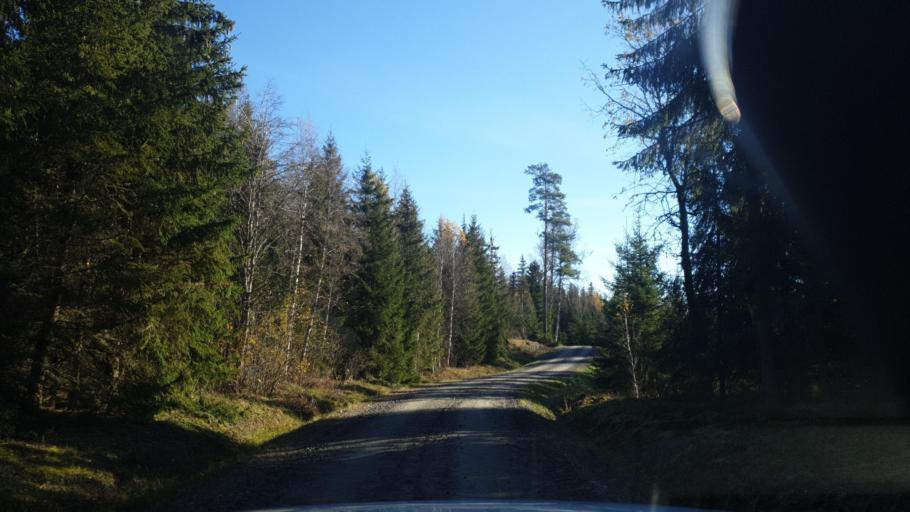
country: SE
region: Vaermland
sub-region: Karlstads Kommun
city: Edsvalla
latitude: 59.4614
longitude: 13.1120
